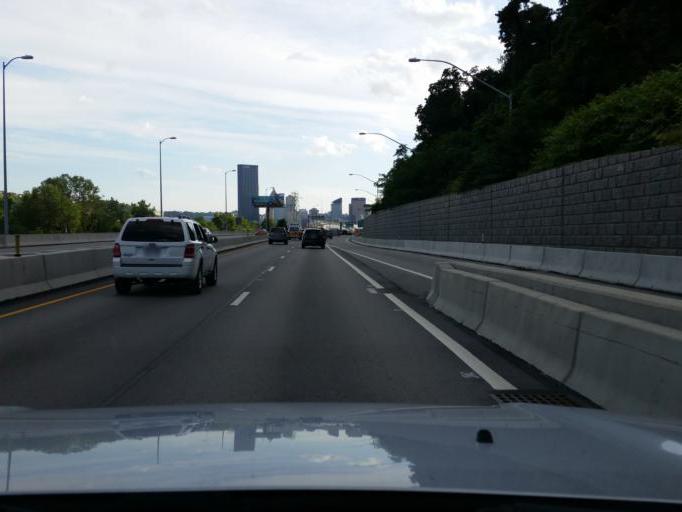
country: US
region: Pennsylvania
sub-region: Allegheny County
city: Millvale
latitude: 40.4637
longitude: -79.9808
